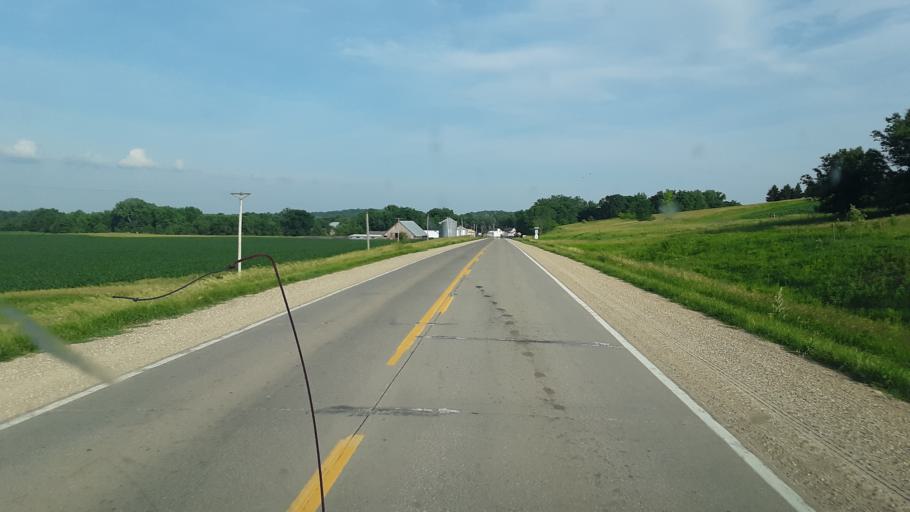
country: US
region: Iowa
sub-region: Tama County
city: Toledo
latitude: 41.9865
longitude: -92.7194
